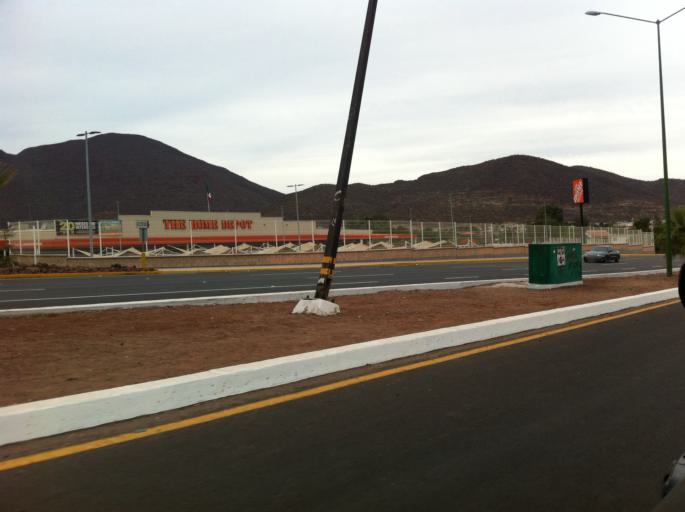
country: MX
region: Sonora
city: Heroica Guaymas
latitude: 27.9396
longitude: -110.9312
